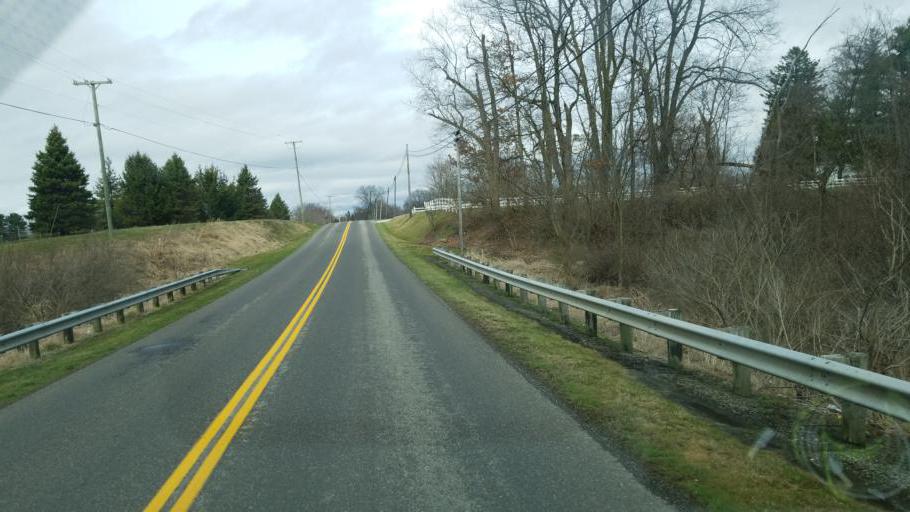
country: US
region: Ohio
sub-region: Wayne County
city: Wooster
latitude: 40.7739
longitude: -81.9632
